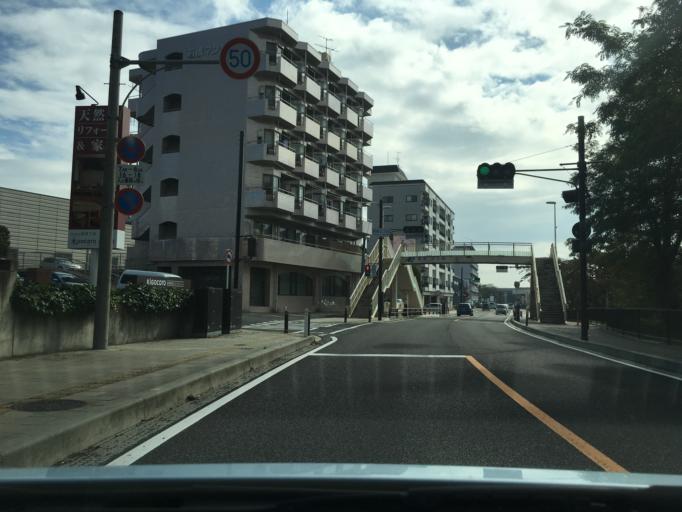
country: JP
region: Fukushima
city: Koriyama
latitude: 37.3808
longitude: 140.3652
